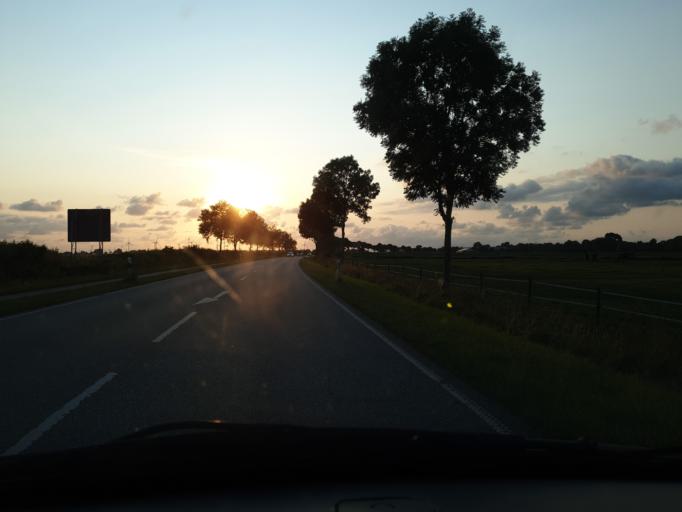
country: DE
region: Schleswig-Holstein
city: Schmedeswurth
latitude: 53.9090
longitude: 9.0597
